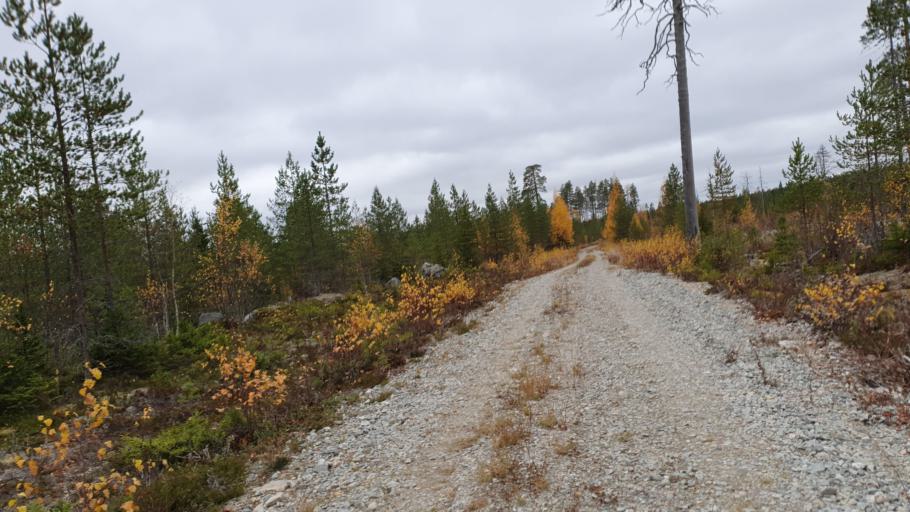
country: FI
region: Kainuu
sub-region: Kehys-Kainuu
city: Kuhmo
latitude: 64.4506
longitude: 29.5934
